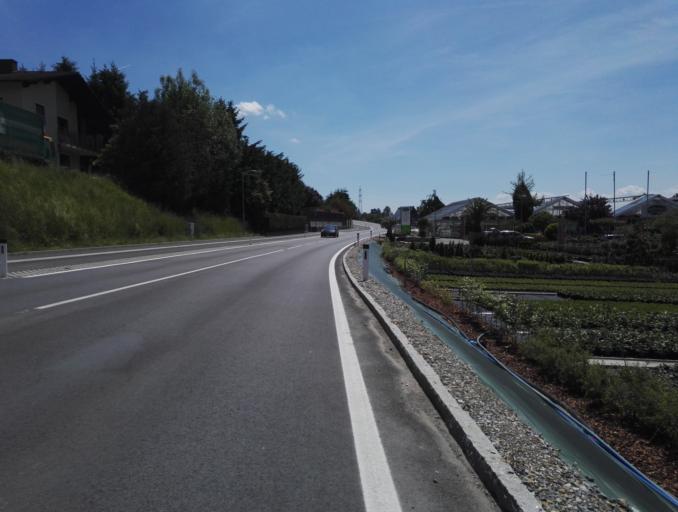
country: AT
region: Styria
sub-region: Politischer Bezirk Graz-Umgebung
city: Grambach
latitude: 47.0241
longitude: 15.4990
